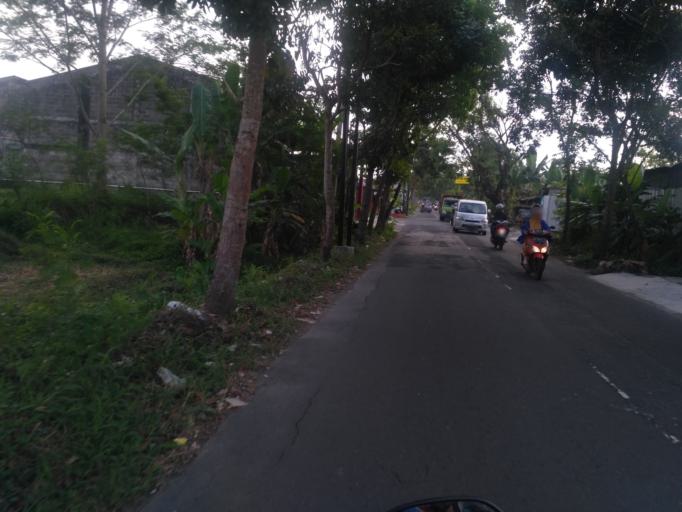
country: ID
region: Daerah Istimewa Yogyakarta
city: Yogyakarta
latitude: -7.7679
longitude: 110.3438
